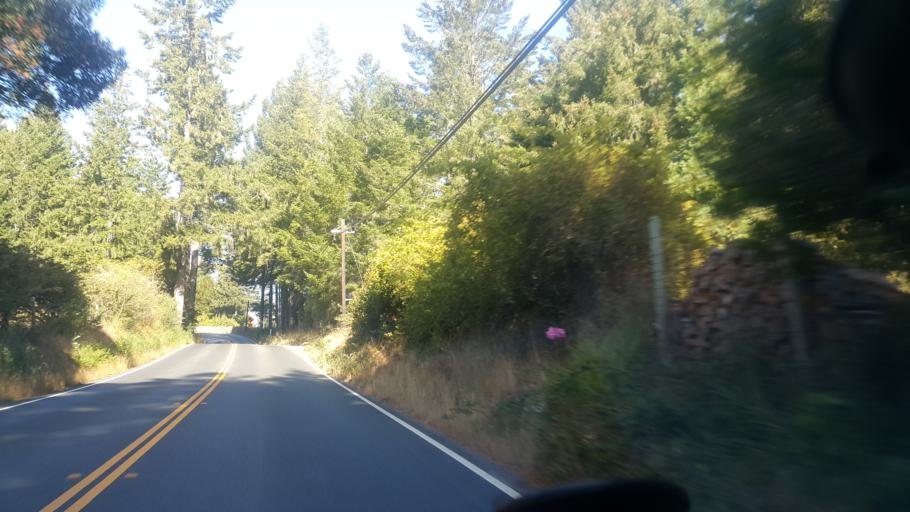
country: US
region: California
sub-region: Mendocino County
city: Fort Bragg
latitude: 39.4069
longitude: -123.7264
